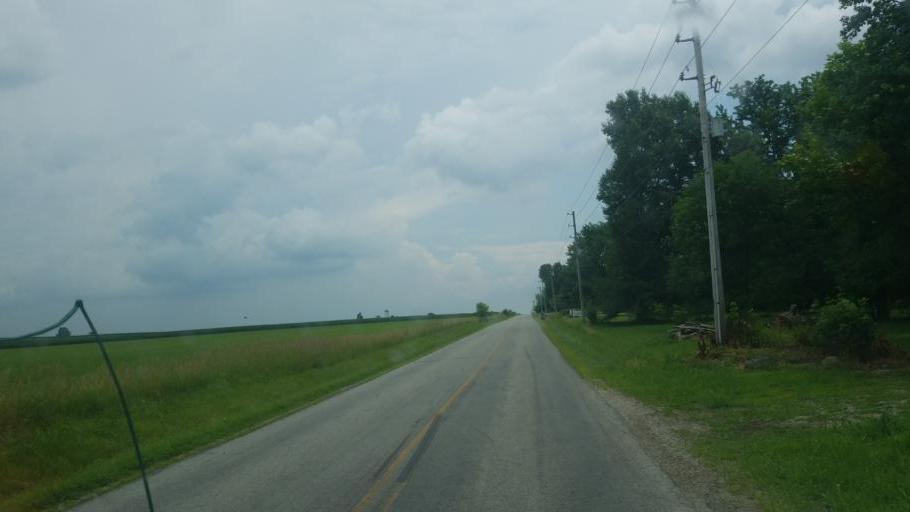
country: US
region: Ohio
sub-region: Wayne County
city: West Salem
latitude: 40.8580
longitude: -82.0536
